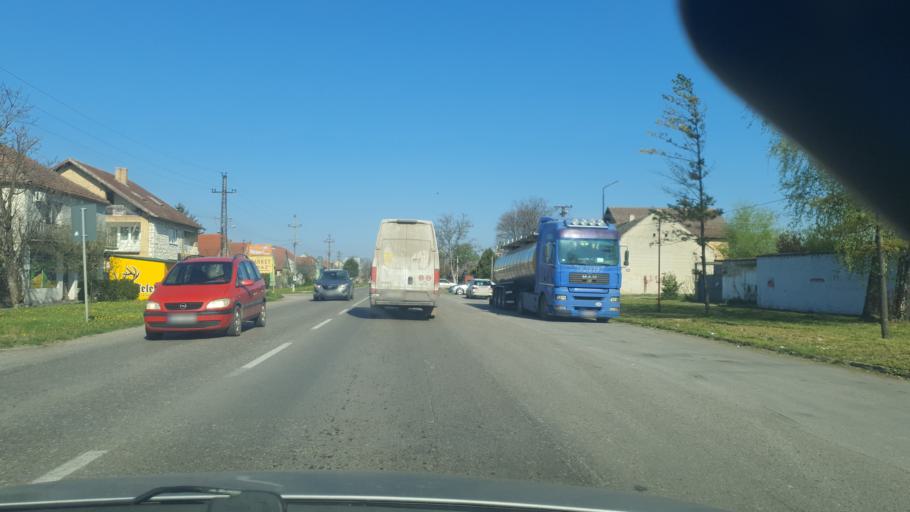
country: RS
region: Autonomna Pokrajina Vojvodina
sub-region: Zapadnobacki Okrug
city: Kula
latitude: 45.6639
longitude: 19.4445
